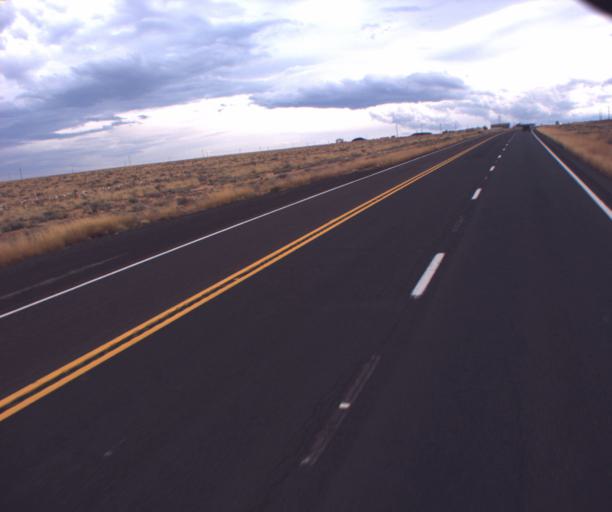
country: US
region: Arizona
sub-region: Coconino County
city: Tuba City
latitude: 35.7619
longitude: -111.4665
